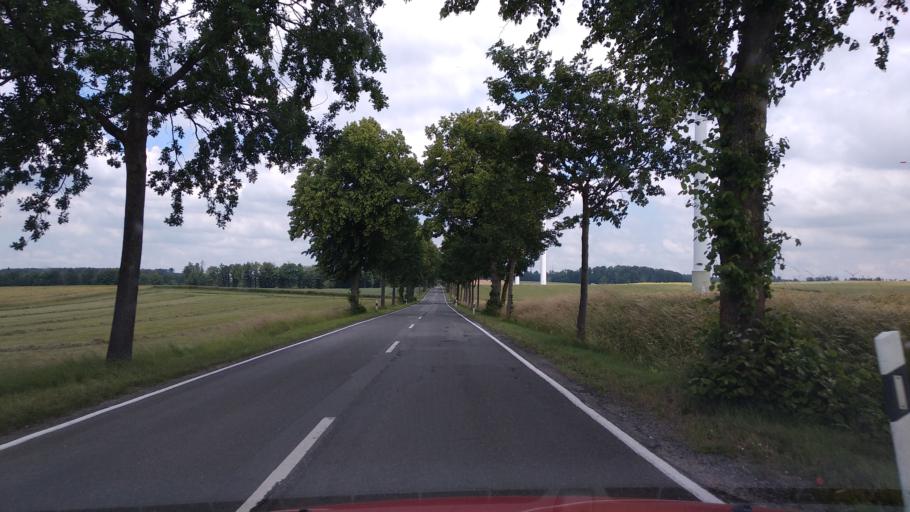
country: DE
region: North Rhine-Westphalia
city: Borgentreich
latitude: 51.5929
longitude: 9.3238
